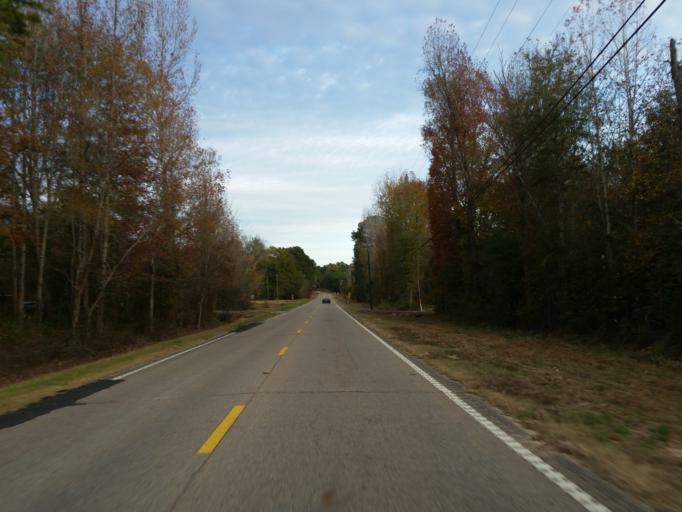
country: US
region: Mississippi
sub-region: Lauderdale County
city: Marion
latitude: 32.4122
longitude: -88.5503
